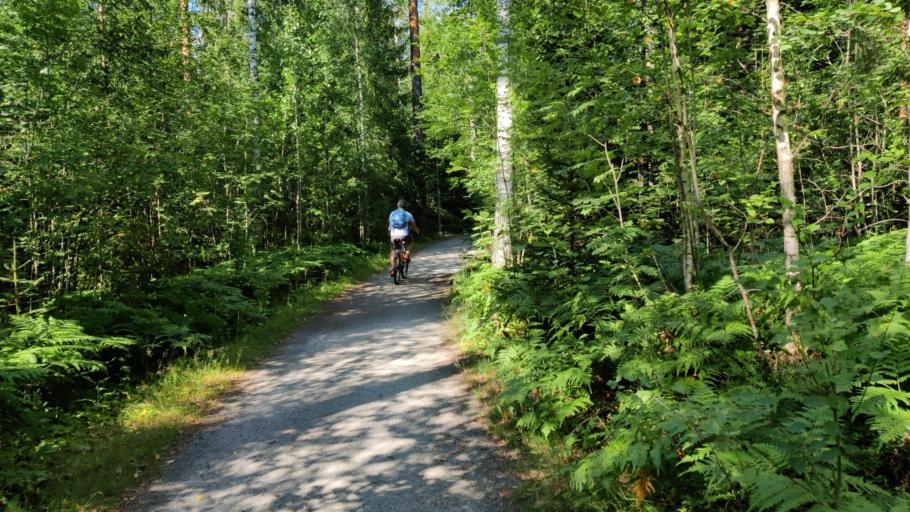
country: FI
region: Uusimaa
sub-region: Helsinki
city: Teekkarikylae
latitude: 60.2536
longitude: 24.8398
